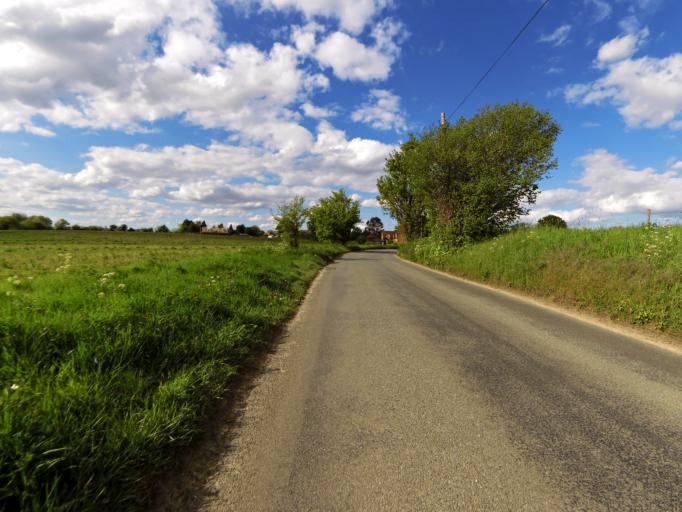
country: GB
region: England
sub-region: Suffolk
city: Woolpit
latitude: 52.2215
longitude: 0.8817
